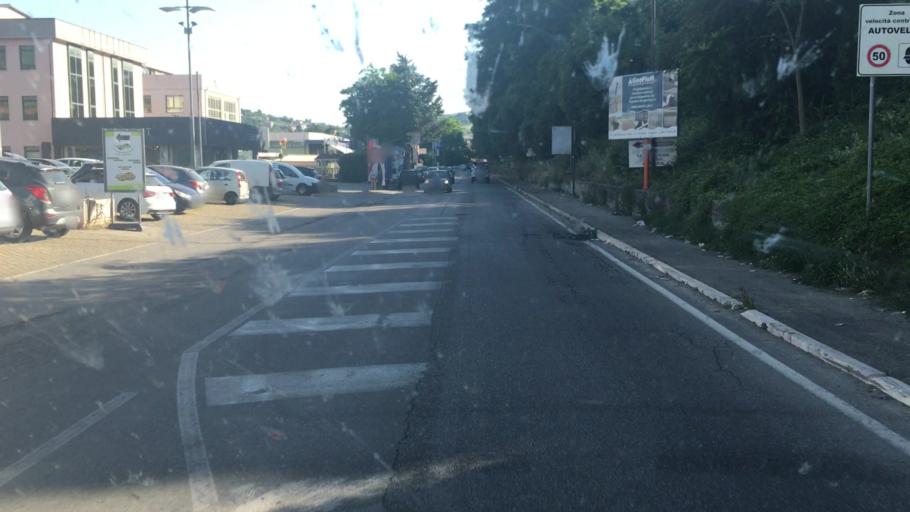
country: IT
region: Basilicate
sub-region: Provincia di Potenza
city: Potenza
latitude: 40.6328
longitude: 15.8125
